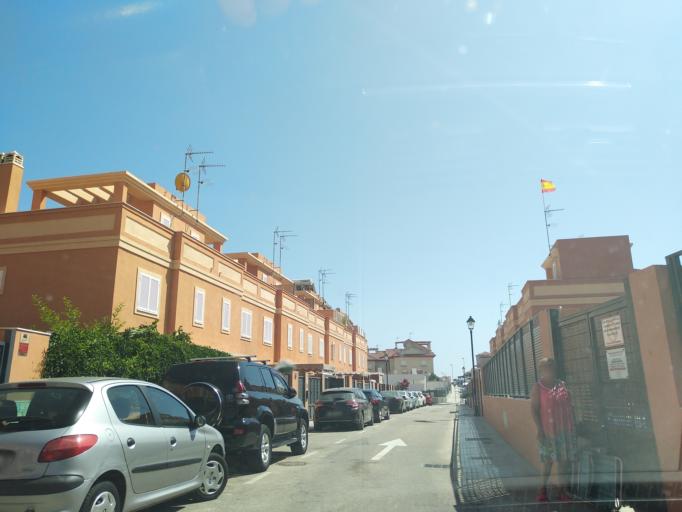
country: ES
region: Andalusia
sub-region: Provincia de Malaga
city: Valdes
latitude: 36.7202
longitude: -4.1980
